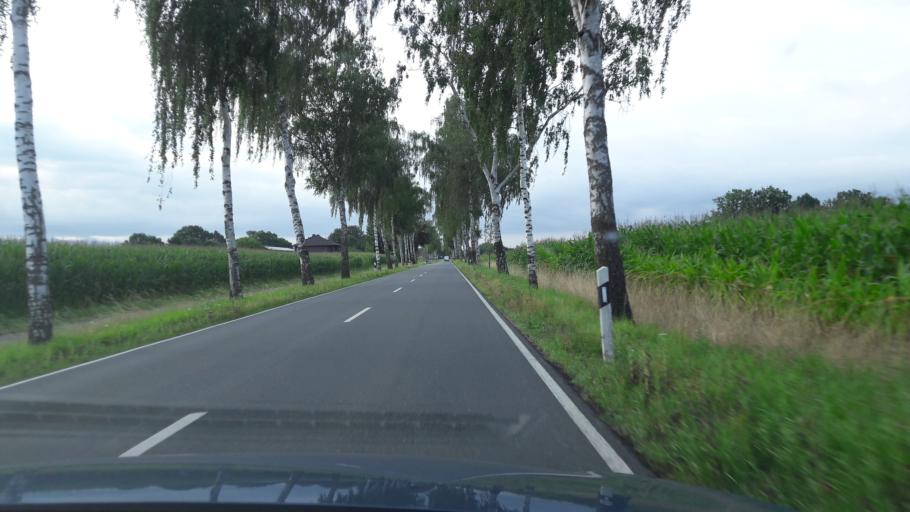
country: DE
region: North Rhine-Westphalia
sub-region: Regierungsbezirk Munster
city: Everswinkel
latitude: 51.8791
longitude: 7.8975
